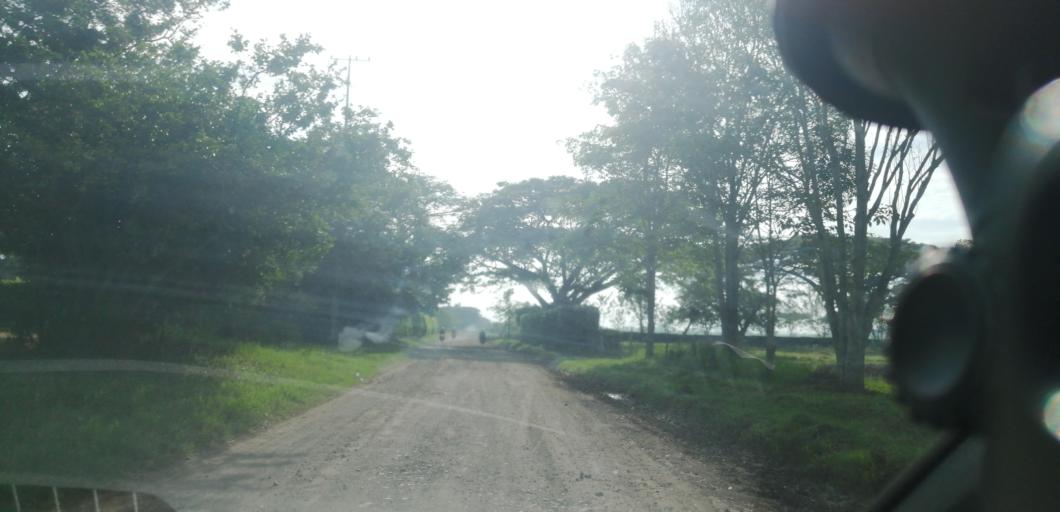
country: CO
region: Valle del Cauca
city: Yumbo
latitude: 3.5799
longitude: -76.4172
